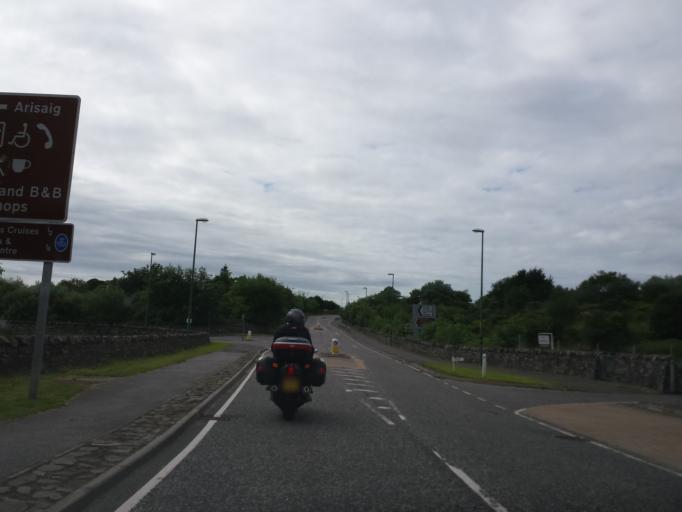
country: GB
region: Scotland
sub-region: Argyll and Bute
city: Isle Of Mull
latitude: 56.9112
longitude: -5.8382
